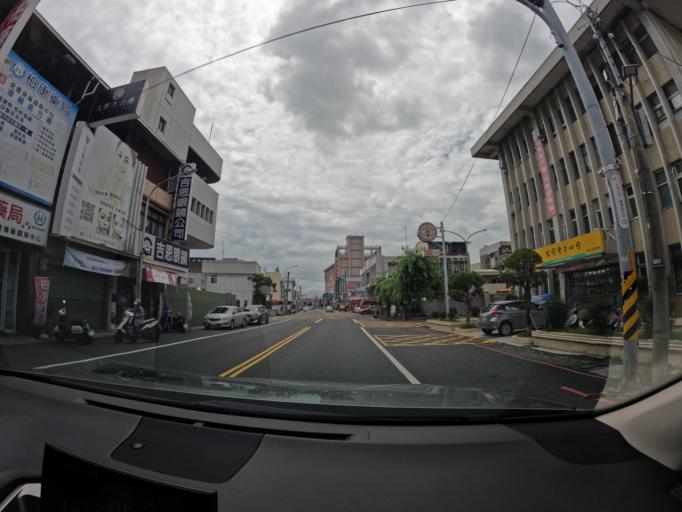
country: TW
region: Kaohsiung
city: Kaohsiung
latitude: 22.7965
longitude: 120.2938
